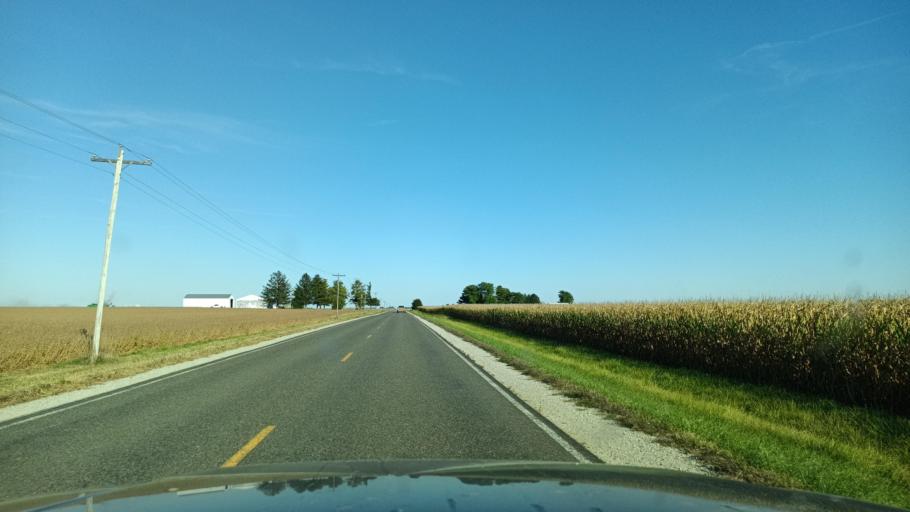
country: US
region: Illinois
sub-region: De Witt County
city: Clinton
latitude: 40.2244
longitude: -88.8795
